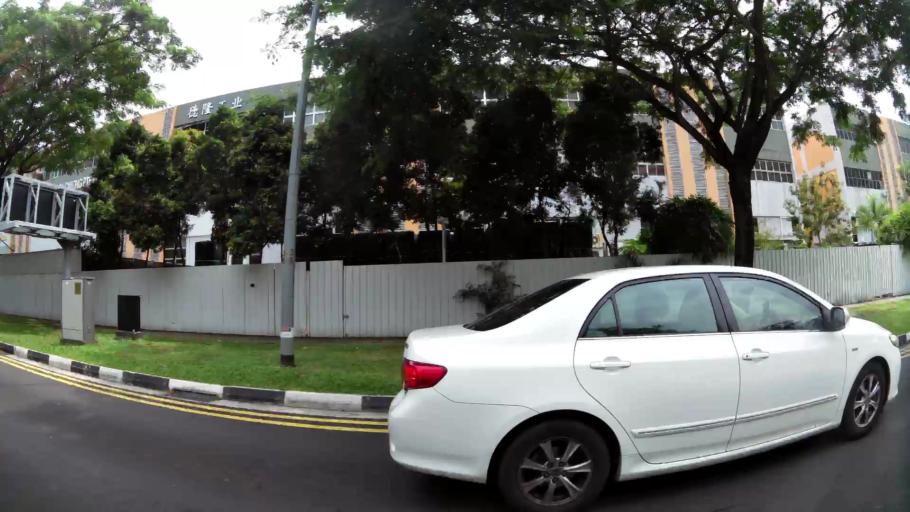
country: SG
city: Singapore
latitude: 1.3363
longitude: 103.8949
